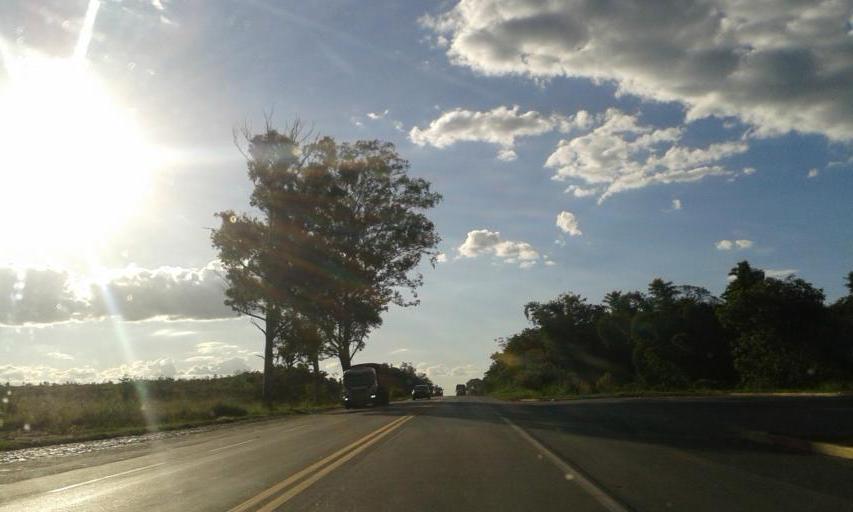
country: BR
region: Minas Gerais
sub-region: Bom Despacho
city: Bom Despacho
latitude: -19.8028
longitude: -45.1344
